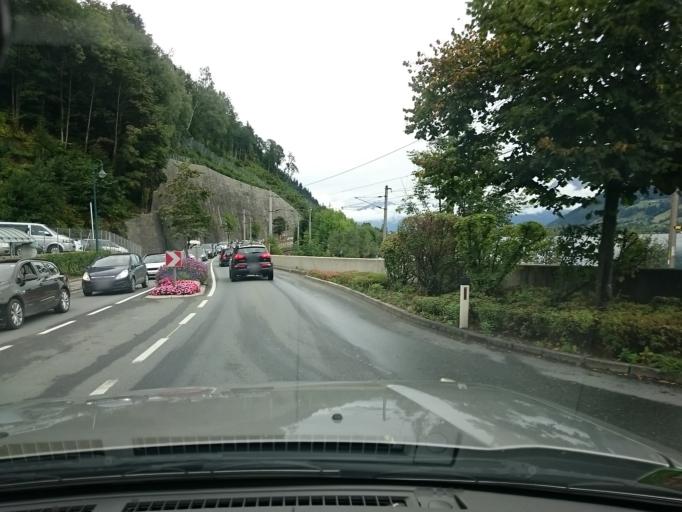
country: AT
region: Salzburg
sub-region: Politischer Bezirk Zell am See
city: Zell am See
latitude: 47.3280
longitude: 12.7967
